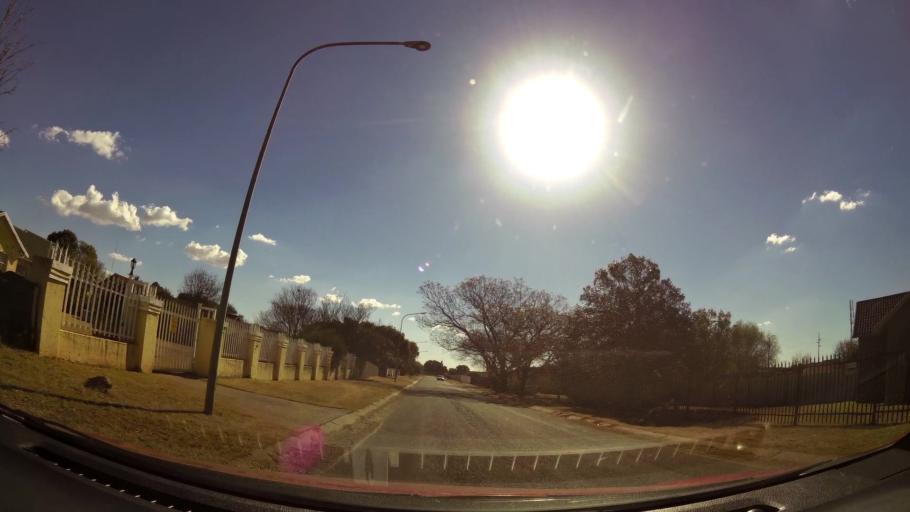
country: ZA
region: Gauteng
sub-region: West Rand District Municipality
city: Carletonville
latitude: -26.3637
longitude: 27.3711
